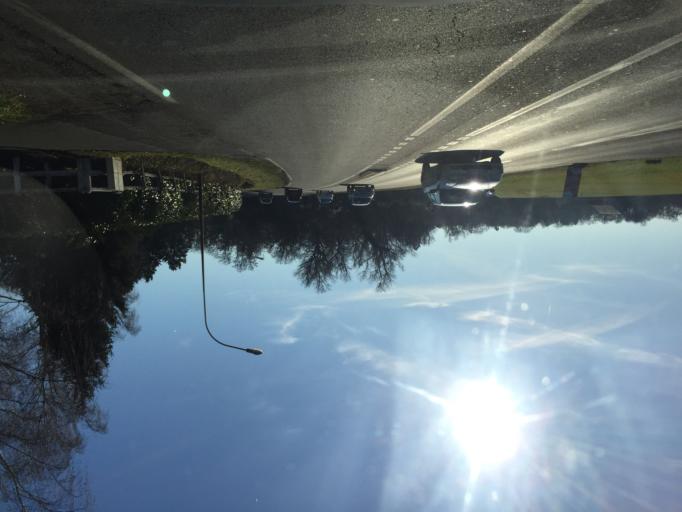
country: FR
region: Auvergne
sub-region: Departement de l'Allier
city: Saint-Remy-en-Rollat
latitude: 46.1653
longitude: 3.3945
